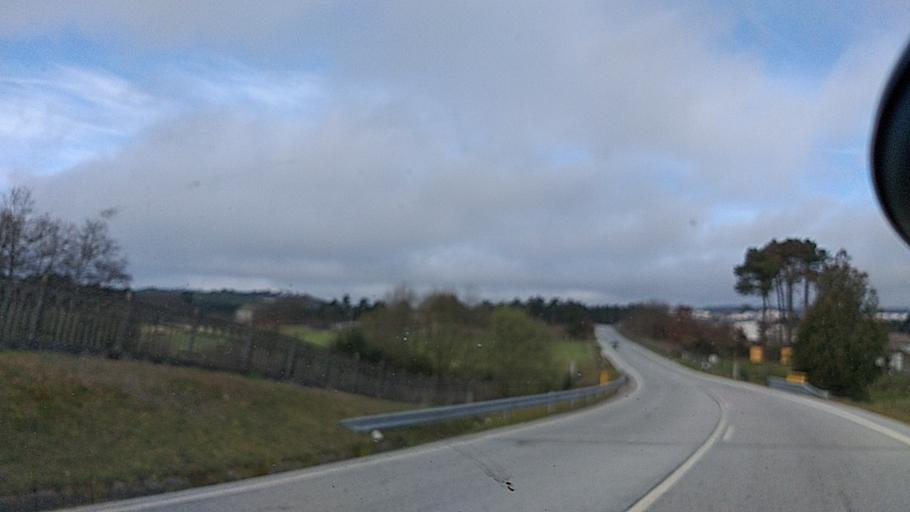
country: PT
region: Guarda
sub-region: Aguiar da Beira
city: Aguiar da Beira
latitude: 40.8067
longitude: -7.5270
